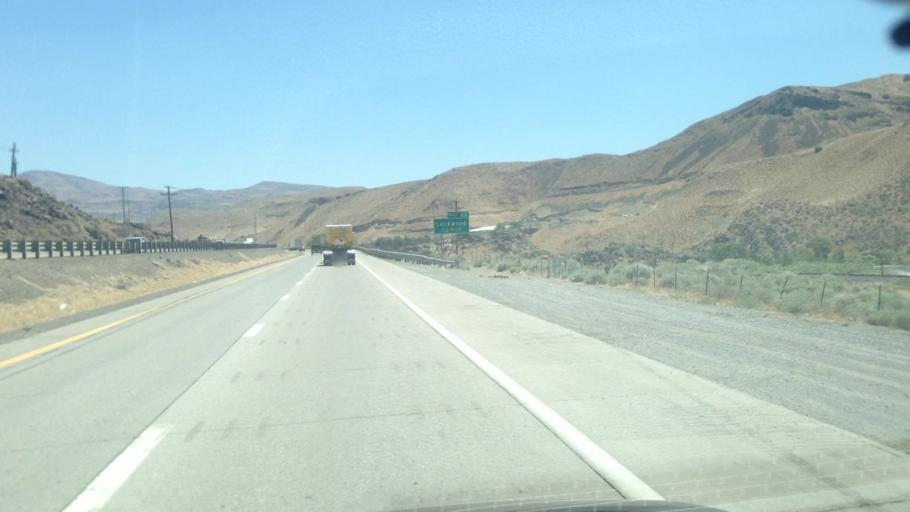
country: US
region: Nevada
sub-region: Washoe County
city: Sparks
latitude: 39.5115
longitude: -119.6684
